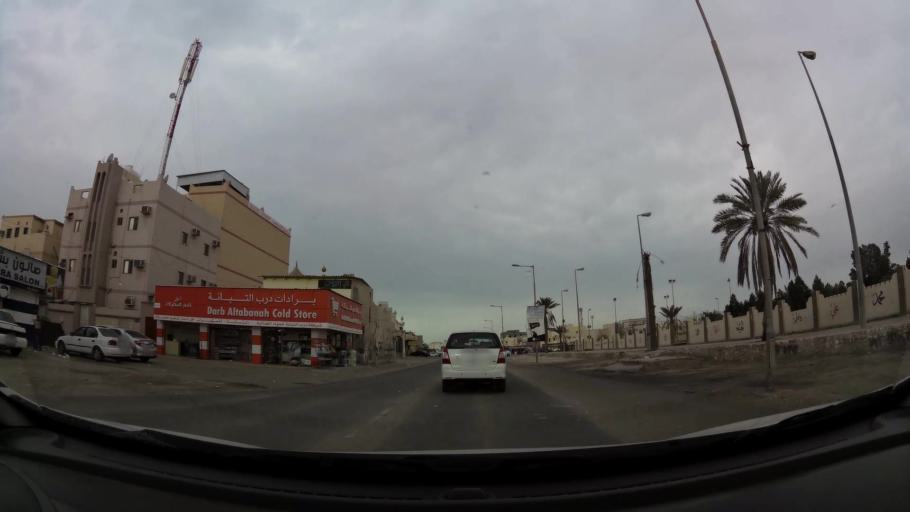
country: BH
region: Central Governorate
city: Madinat Hamad
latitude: 26.1245
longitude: 50.4775
